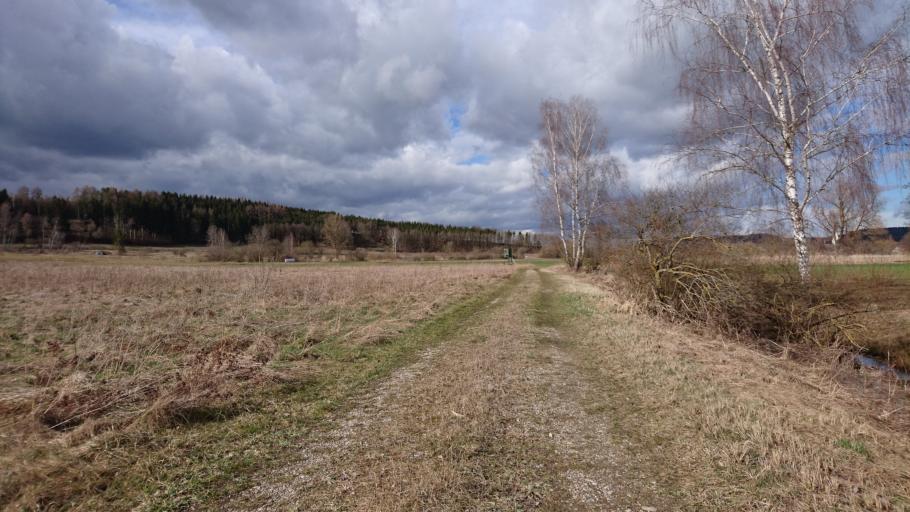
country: DE
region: Bavaria
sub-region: Swabia
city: Zusmarshausen
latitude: 48.4297
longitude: 10.5897
